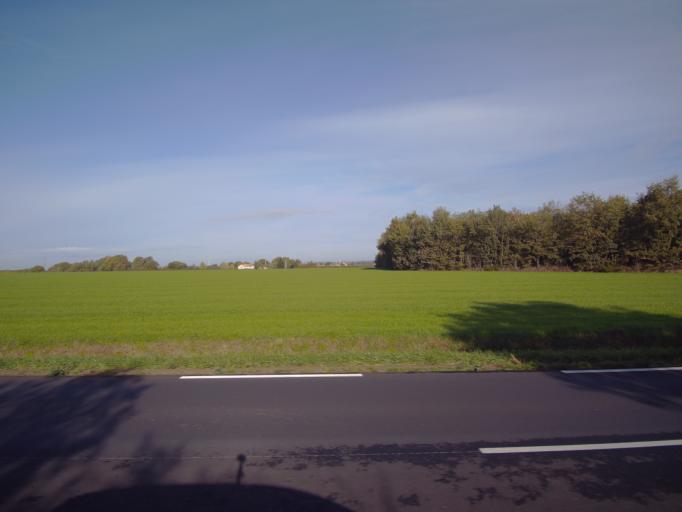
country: FR
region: Pays de la Loire
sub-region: Departement de Maine-et-Loire
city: Nueil-sur-Layon
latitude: 47.1572
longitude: -0.4163
